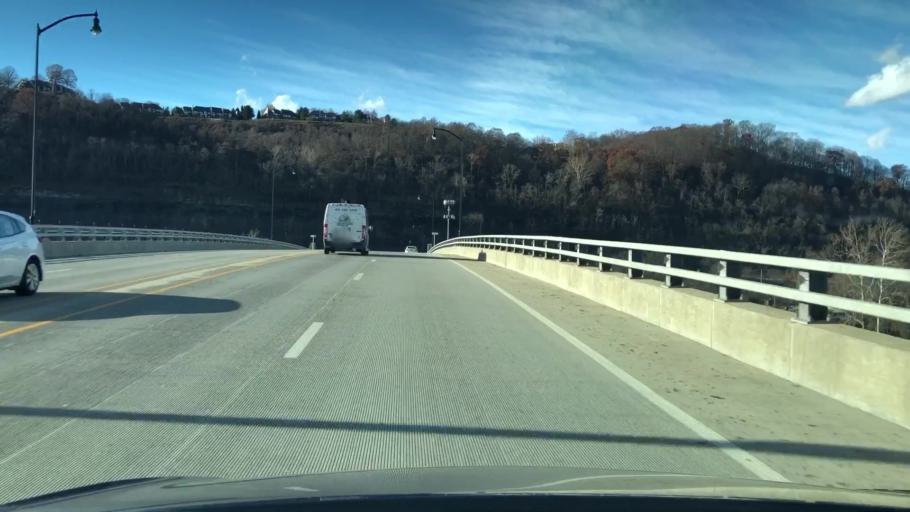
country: US
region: Pennsylvania
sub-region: Allegheny County
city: Oakmont
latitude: 40.5270
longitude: -79.8453
